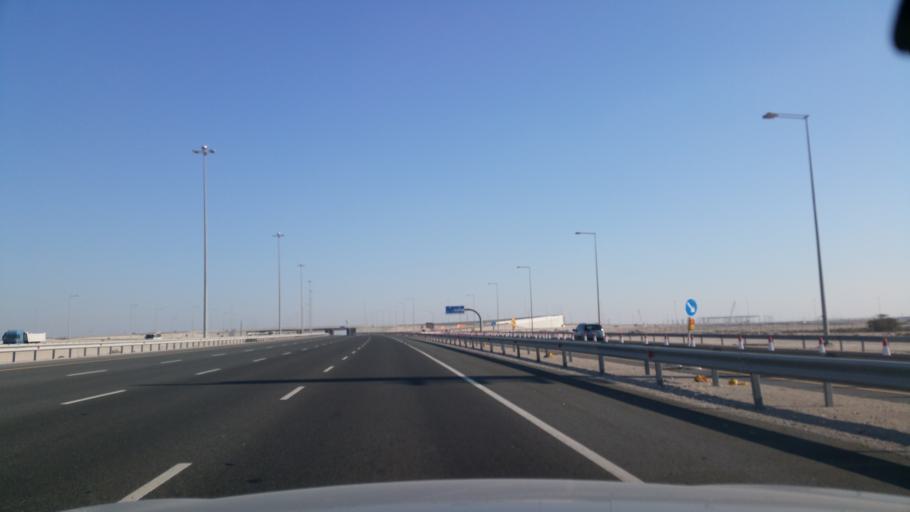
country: QA
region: Al Wakrah
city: Al Wukayr
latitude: 25.1288
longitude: 51.4819
